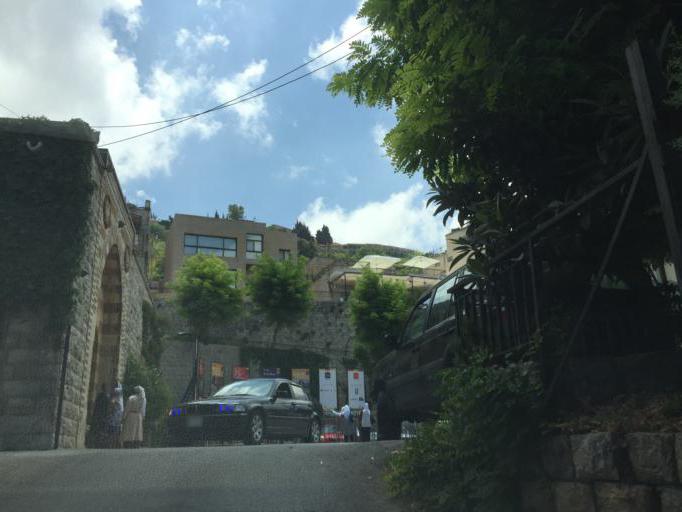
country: LB
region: Mont-Liban
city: Beit ed Dine
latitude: 33.6951
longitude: 35.5803
